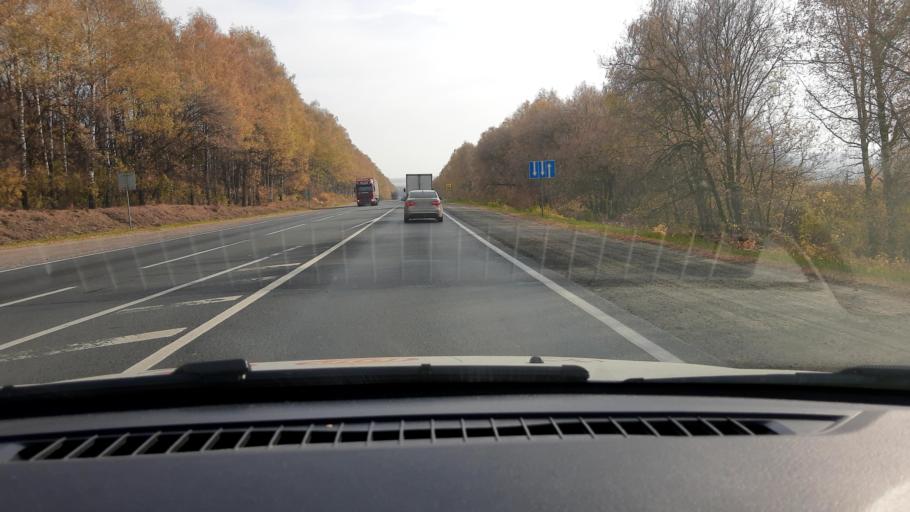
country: RU
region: Nizjnij Novgorod
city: Pamyat' Parizhskoy Kommuny
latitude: 56.0548
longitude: 44.4022
